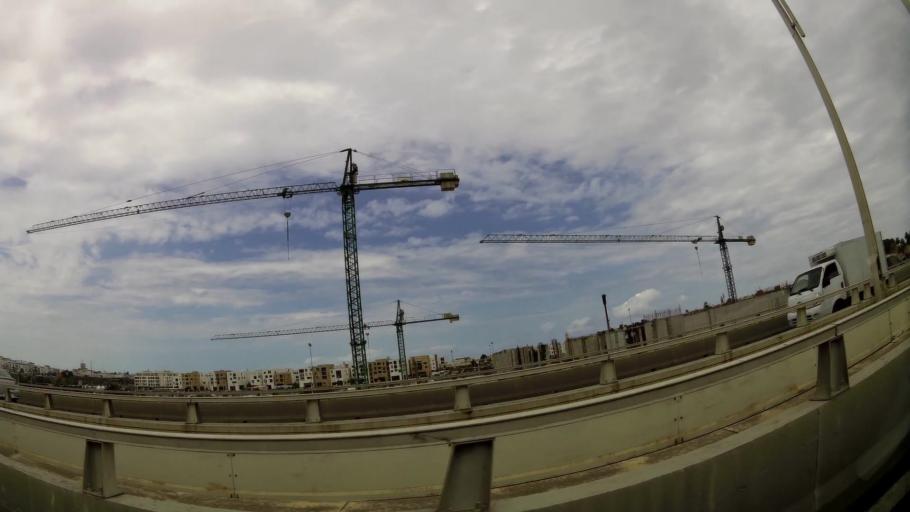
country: MA
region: Rabat-Sale-Zemmour-Zaer
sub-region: Rabat
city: Rabat
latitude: 34.0306
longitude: -6.8186
